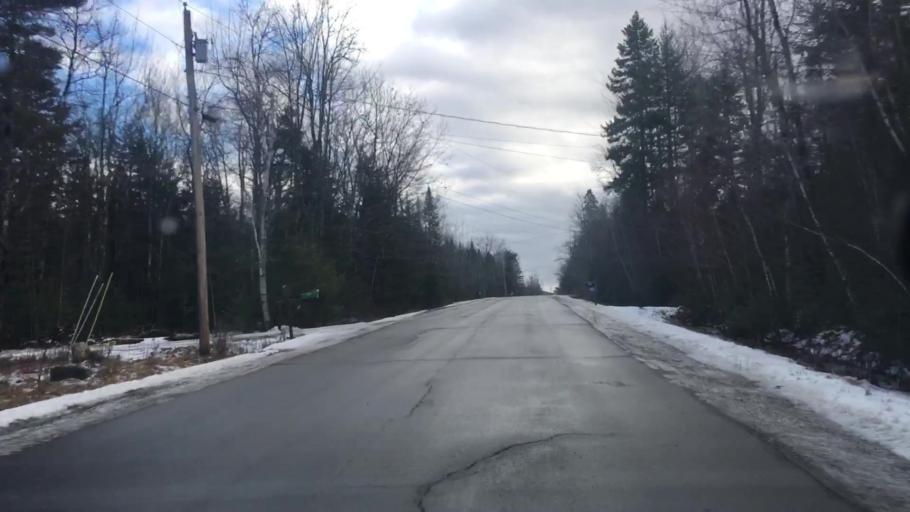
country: US
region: Maine
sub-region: Hancock County
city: Dedham
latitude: 44.6785
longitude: -68.7043
